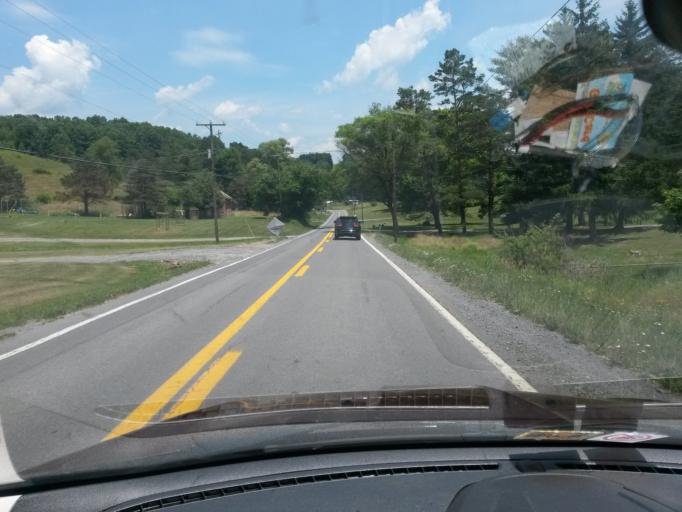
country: US
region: Virginia
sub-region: Giles County
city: Pembroke
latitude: 37.4598
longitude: -80.6619
